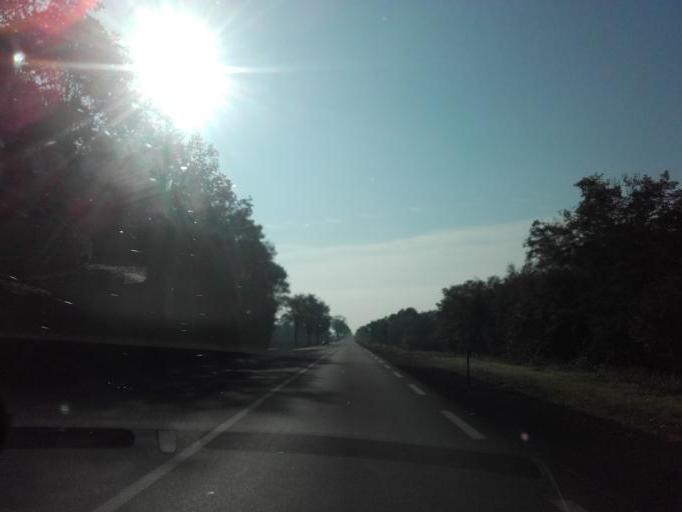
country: FR
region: Bourgogne
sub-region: Departement de Saone-et-Loire
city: Fontaines
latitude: 46.8688
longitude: 4.7915
